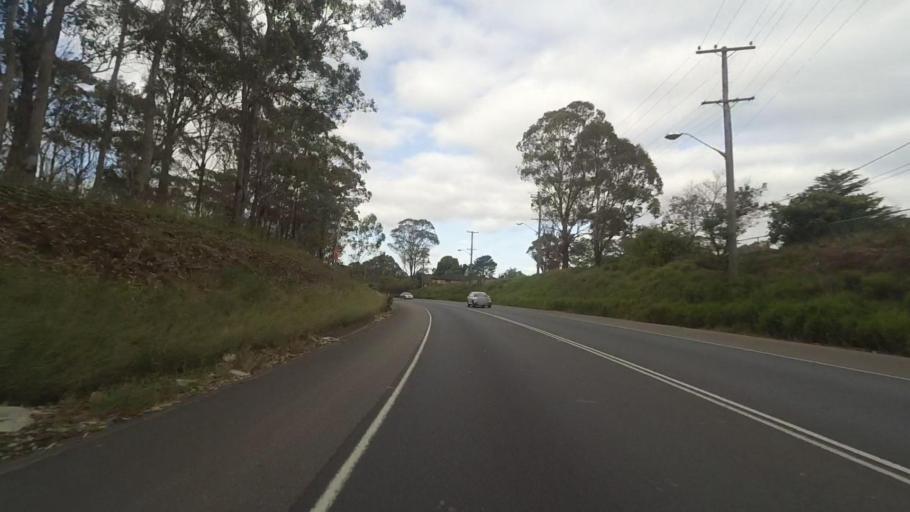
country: AU
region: New South Wales
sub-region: Bankstown
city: Milperra
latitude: -33.9100
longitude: 150.9803
